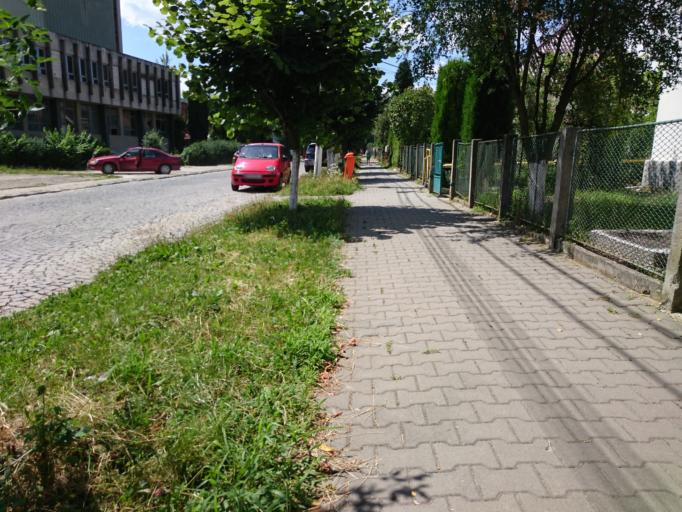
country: RO
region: Mures
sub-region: Municipiul Sighisoara
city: Sighisoara
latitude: 46.2253
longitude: 24.7978
